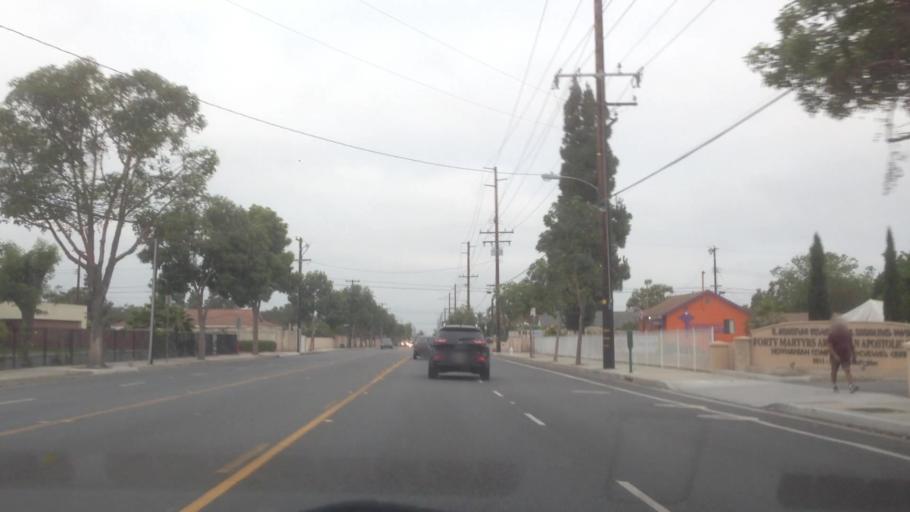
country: US
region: California
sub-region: Orange County
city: Fountain Valley
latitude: 33.7382
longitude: -117.9385
